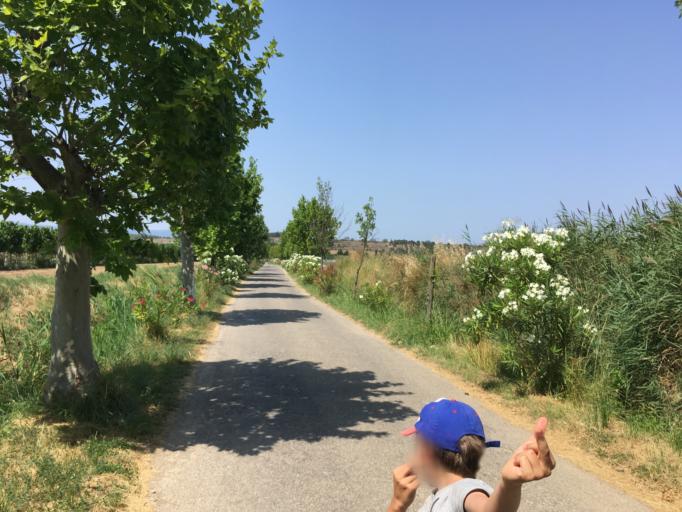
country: FR
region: Languedoc-Roussillon
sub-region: Departement de l'Aude
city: Puicheric
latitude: 43.2262
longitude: 2.6224
